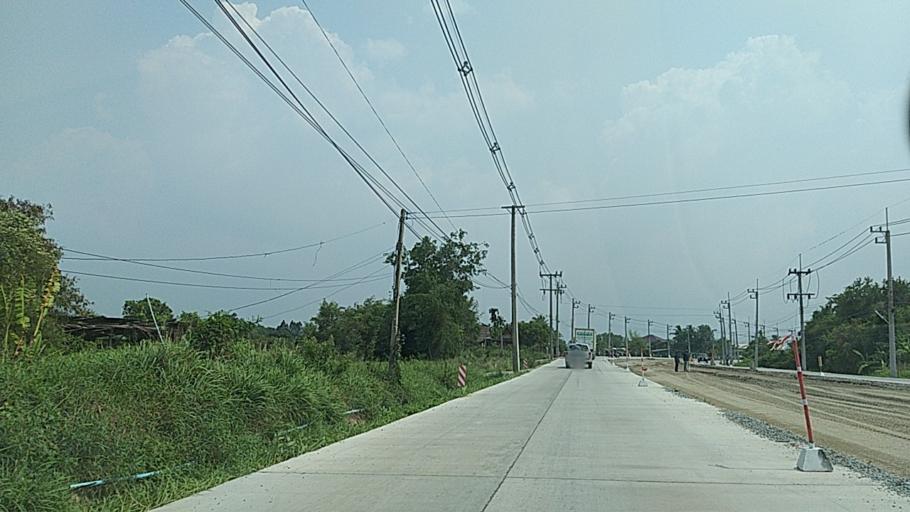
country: TH
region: Chon Buri
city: Phanat Nikhom
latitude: 13.3950
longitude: 101.1919
